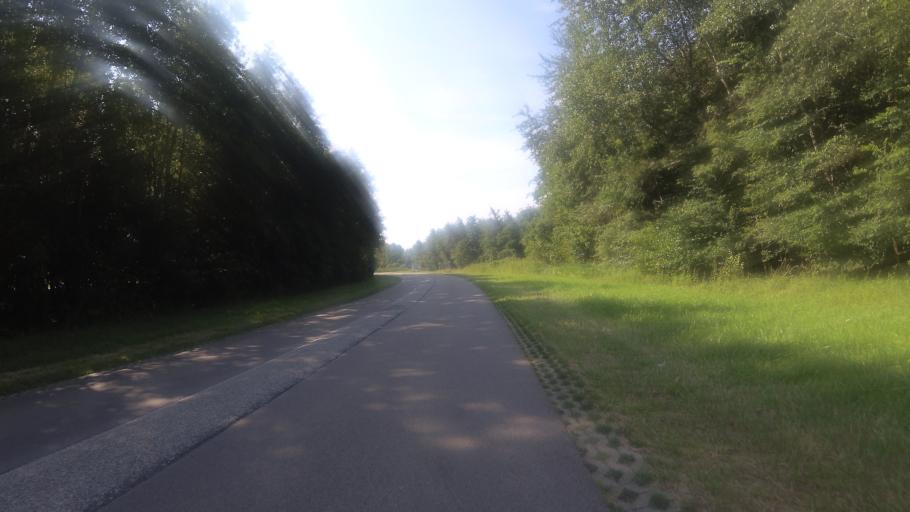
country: NL
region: Zeeland
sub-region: Gemeente Veere
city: Veere
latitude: 51.5755
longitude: 3.6610
